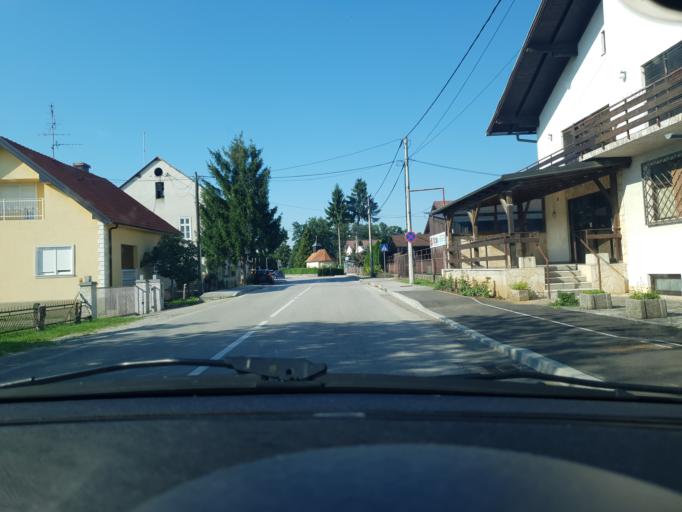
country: HR
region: Zagrebacka
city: Jablanovec
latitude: 45.9027
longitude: 15.8533
